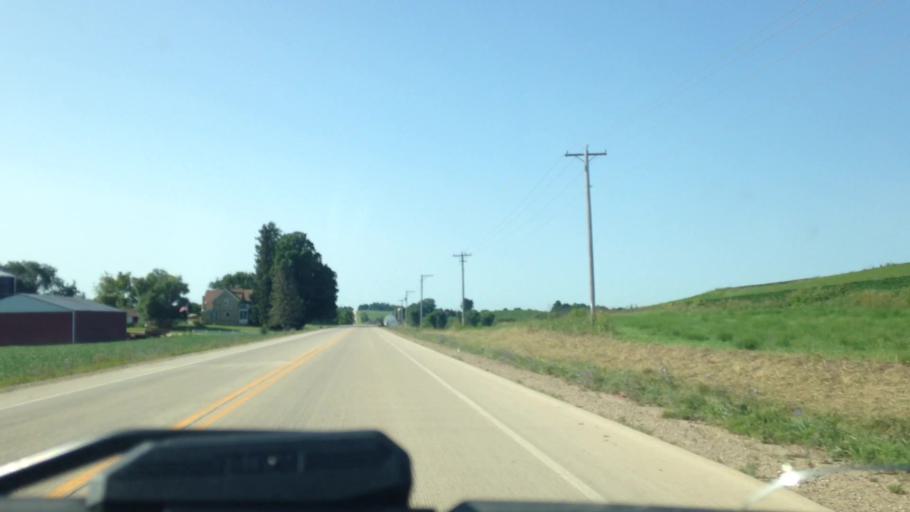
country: US
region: Wisconsin
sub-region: Dodge County
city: Mayville
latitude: 43.4525
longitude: -88.5622
